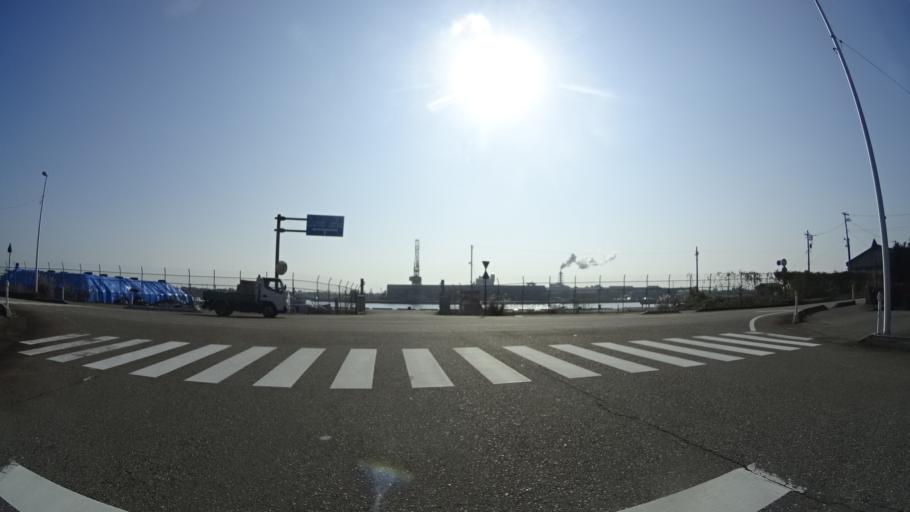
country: JP
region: Toyama
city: Nishishinminato
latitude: 36.7938
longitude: 137.0624
